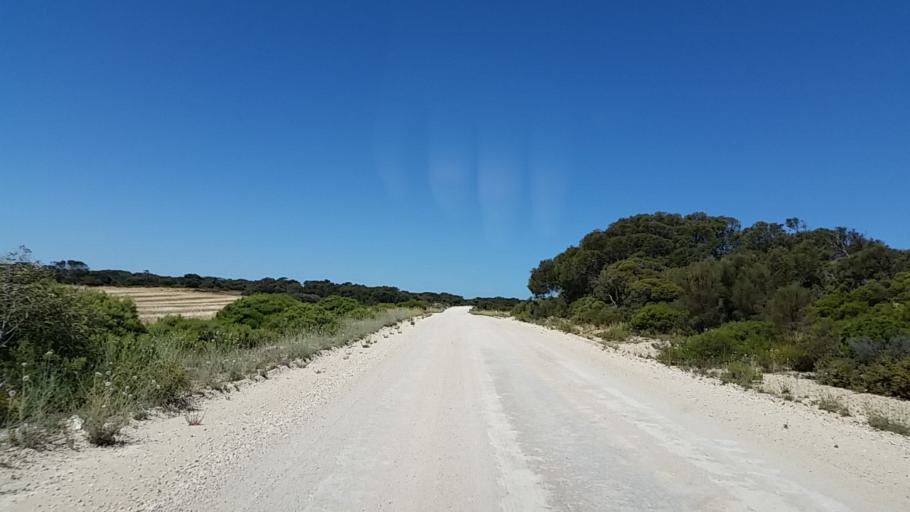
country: AU
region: South Australia
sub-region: Yorke Peninsula
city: Honiton
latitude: -35.2202
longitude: 137.0796
